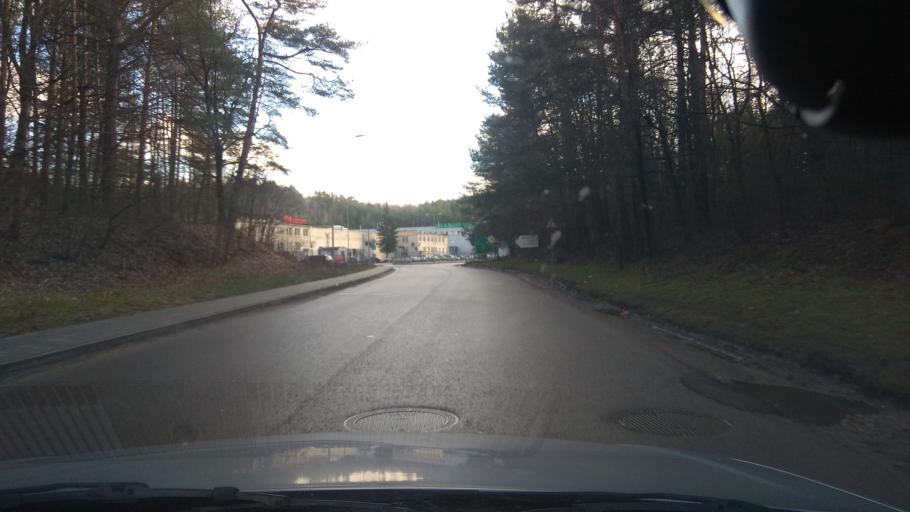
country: LT
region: Vilnius County
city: Lazdynai
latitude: 54.6449
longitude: 25.2205
